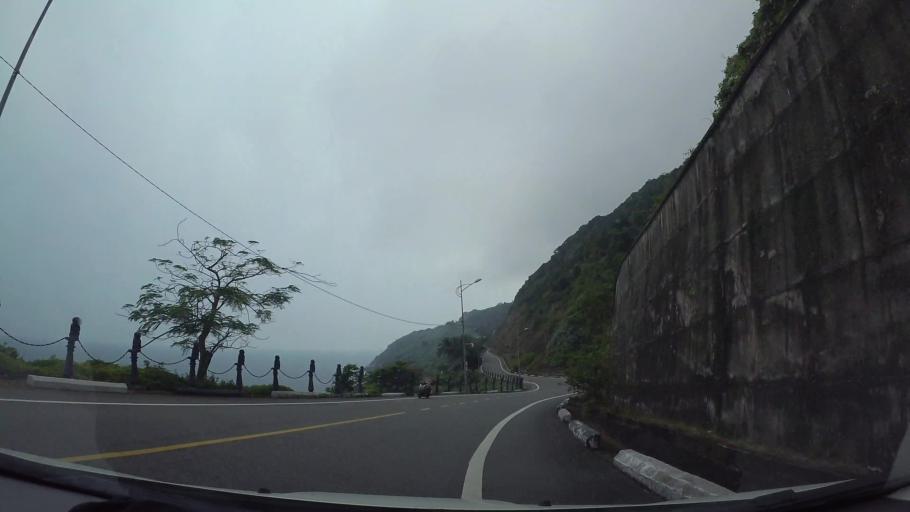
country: VN
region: Da Nang
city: Son Tra
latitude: 16.1107
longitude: 108.3086
